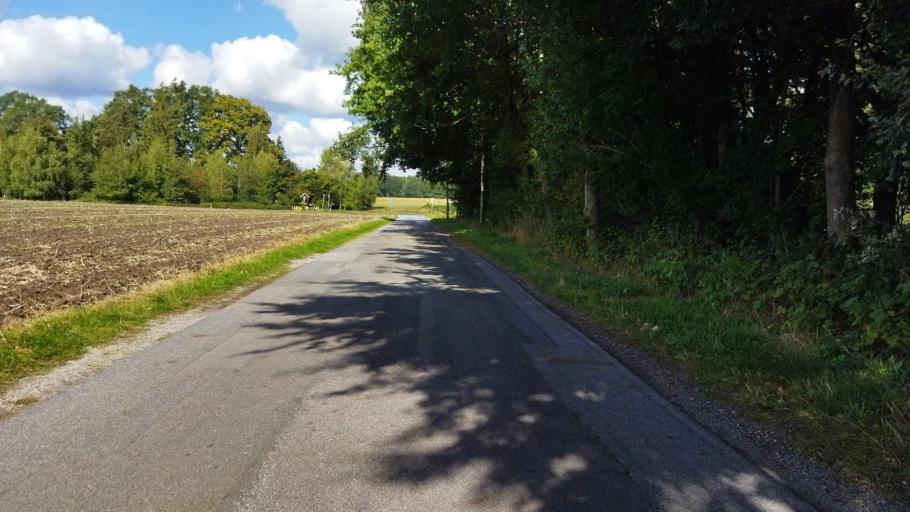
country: DE
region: Lower Saxony
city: Emsburen
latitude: 52.3998
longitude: 7.3223
